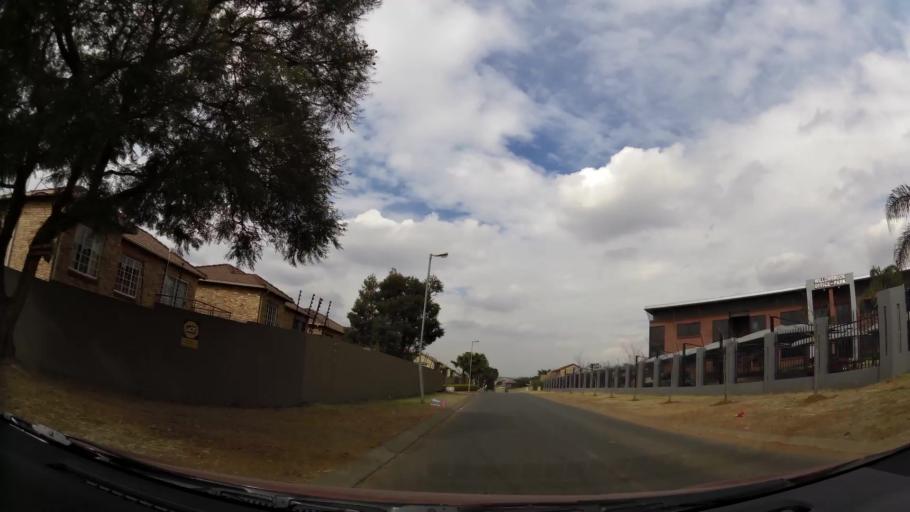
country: ZA
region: Gauteng
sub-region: City of Johannesburg Metropolitan Municipality
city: Roodepoort
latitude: -26.0968
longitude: 27.8766
